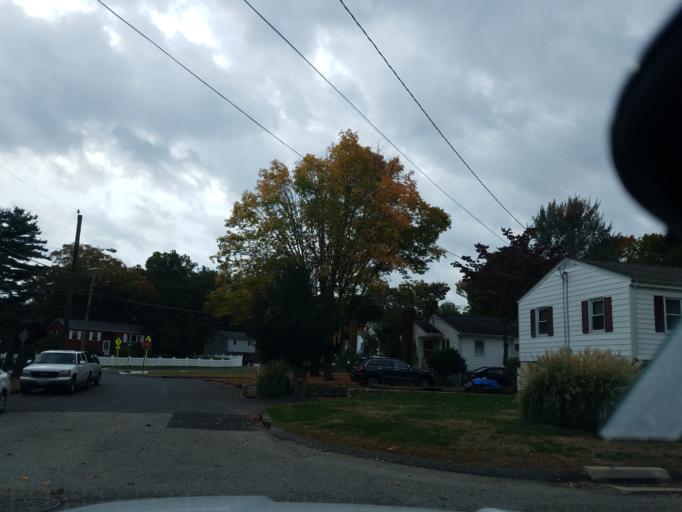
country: US
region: Connecticut
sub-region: Fairfield County
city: Stamford
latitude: 41.0778
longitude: -73.5454
